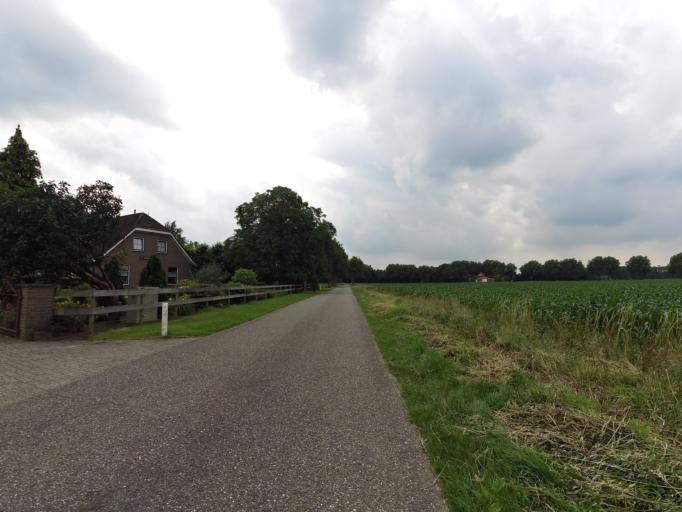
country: NL
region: Gelderland
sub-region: Gemeente Zevenaar
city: Zevenaar
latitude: 51.9177
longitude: 6.1536
